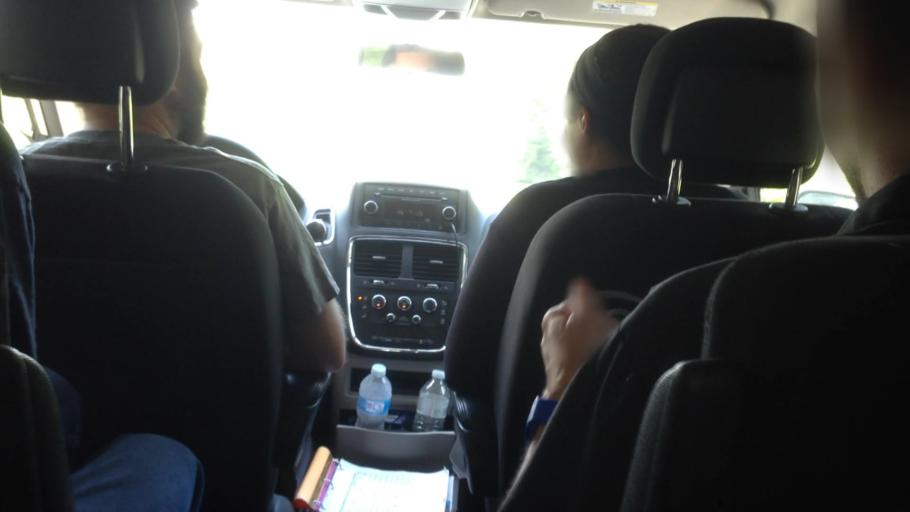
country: US
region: New York
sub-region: Dutchess County
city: Tivoli
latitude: 42.1165
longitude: -73.8912
